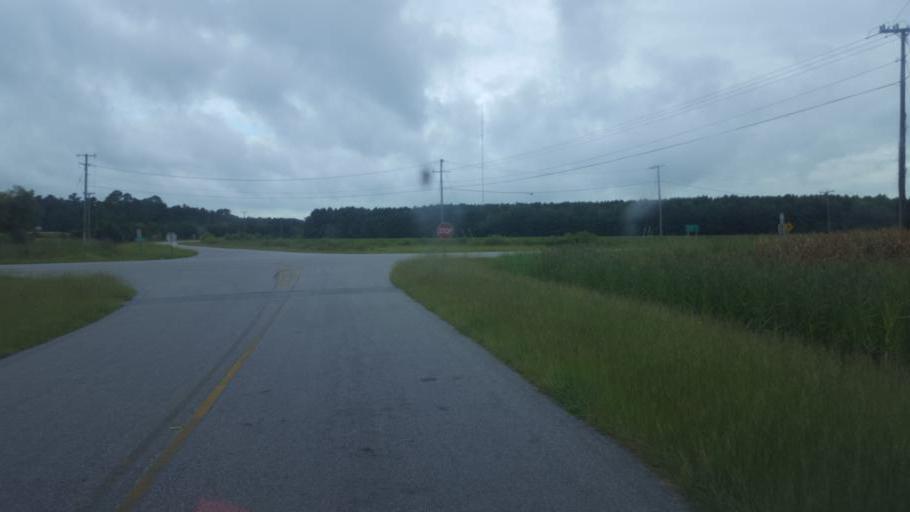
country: US
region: North Carolina
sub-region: Tyrrell County
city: Columbia
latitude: 35.9057
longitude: -76.3201
